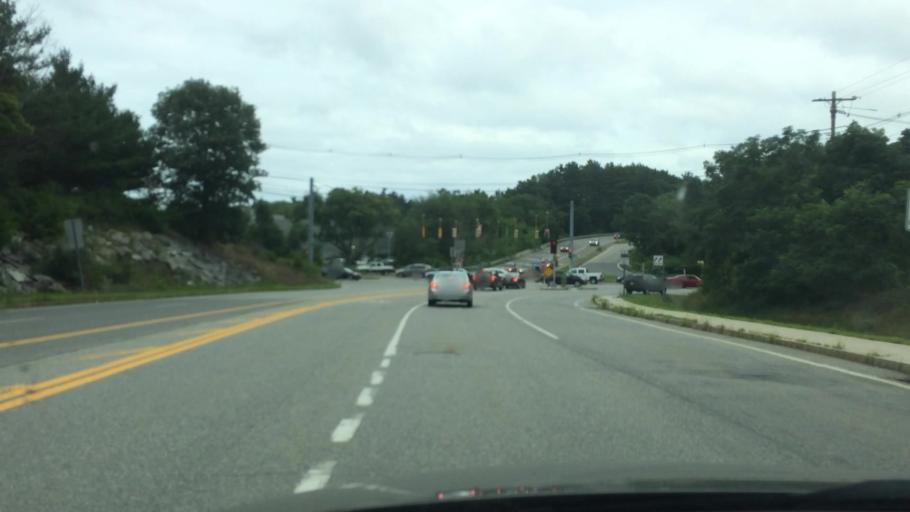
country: US
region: Massachusetts
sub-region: Middlesex County
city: Pinehurst
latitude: 42.5034
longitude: -71.2413
